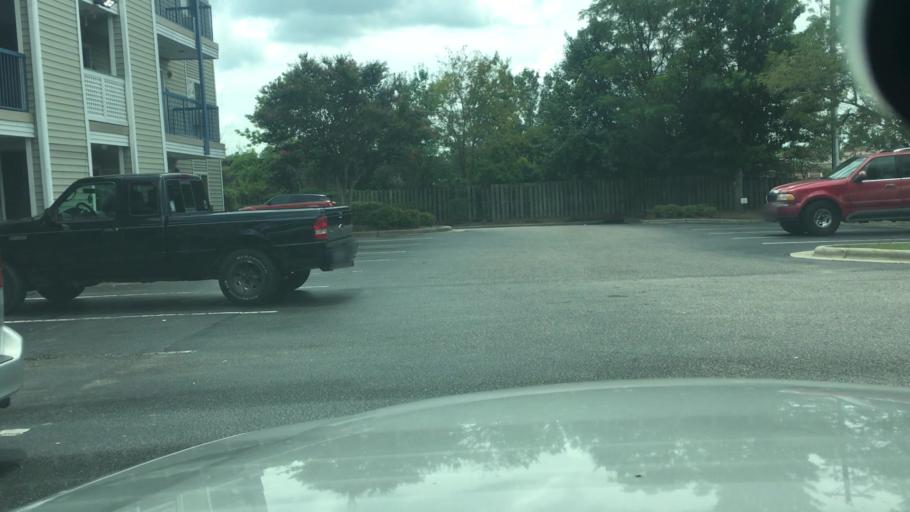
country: US
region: North Carolina
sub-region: Cumberland County
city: Fayetteville
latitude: 35.0800
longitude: -78.9428
